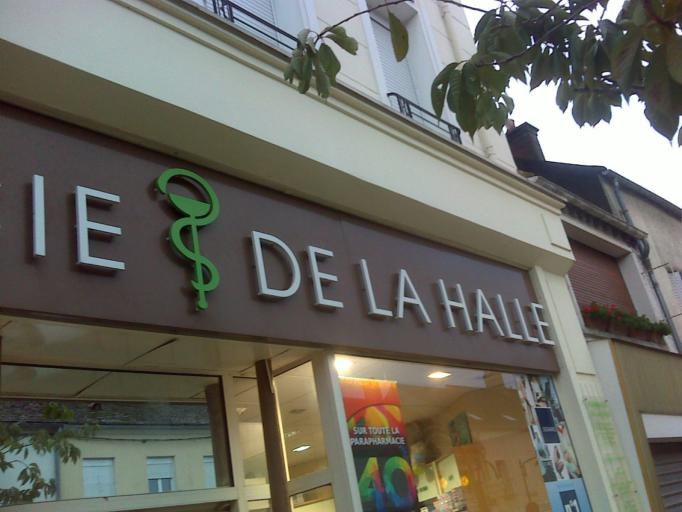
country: FR
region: Ile-de-France
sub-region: Departement de Seine-et-Marne
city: Nangis
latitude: 48.5564
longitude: 3.0121
